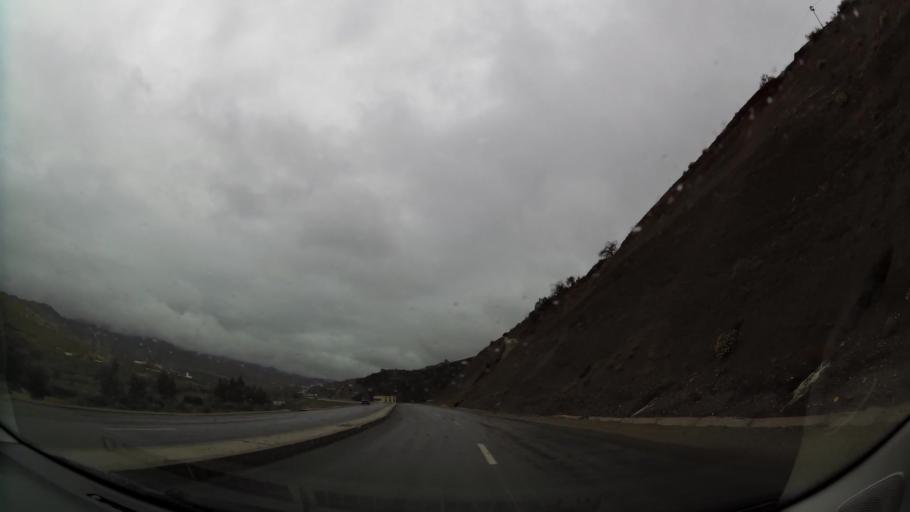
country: MA
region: Taza-Al Hoceima-Taounate
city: Imzourene
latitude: 35.0041
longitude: -3.8123
